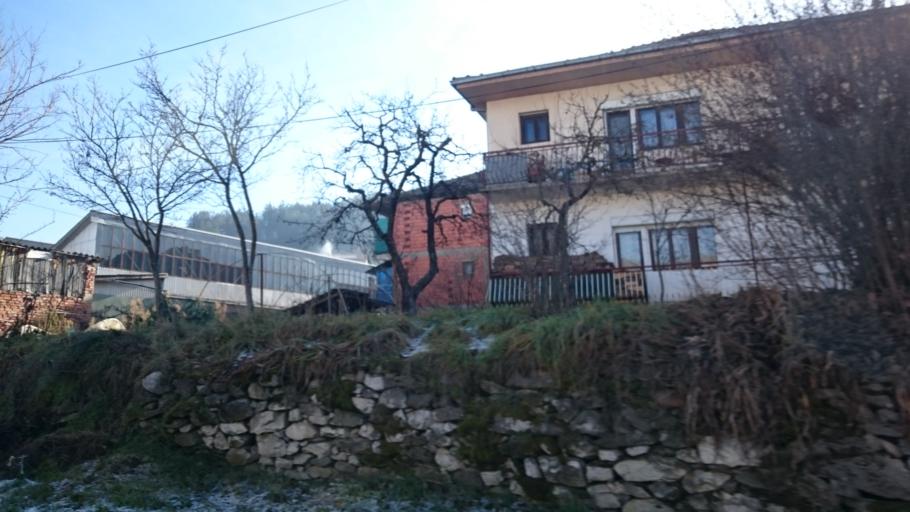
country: MK
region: Makedonski Brod
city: Makedonski Brod
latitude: 41.5075
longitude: 21.2201
